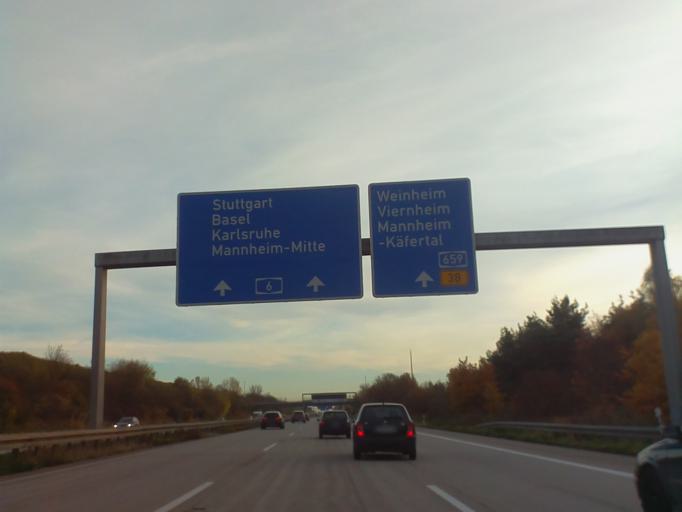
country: DE
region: Hesse
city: Viernheim
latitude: 49.5402
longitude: 8.5590
